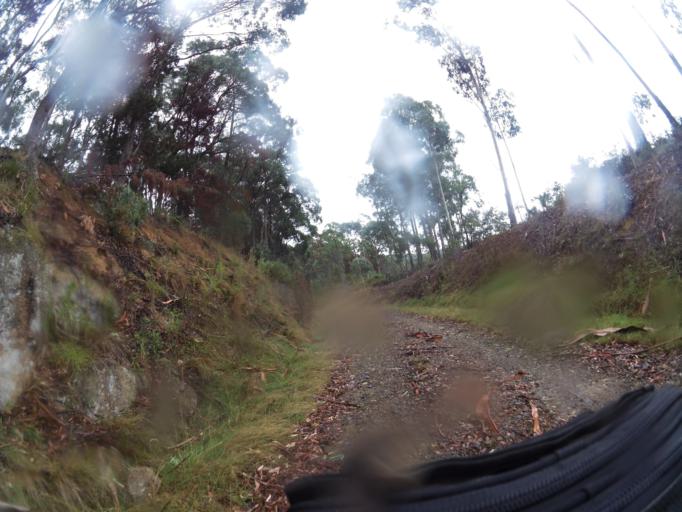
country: AU
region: New South Wales
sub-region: Greater Hume Shire
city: Holbrook
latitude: -36.2243
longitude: 147.5698
